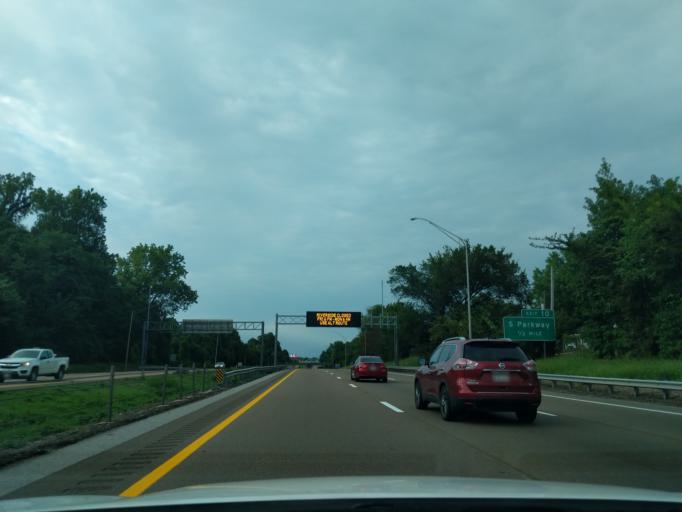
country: US
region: Tennessee
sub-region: Shelby County
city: New South Memphis
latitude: 35.0977
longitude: -90.0763
